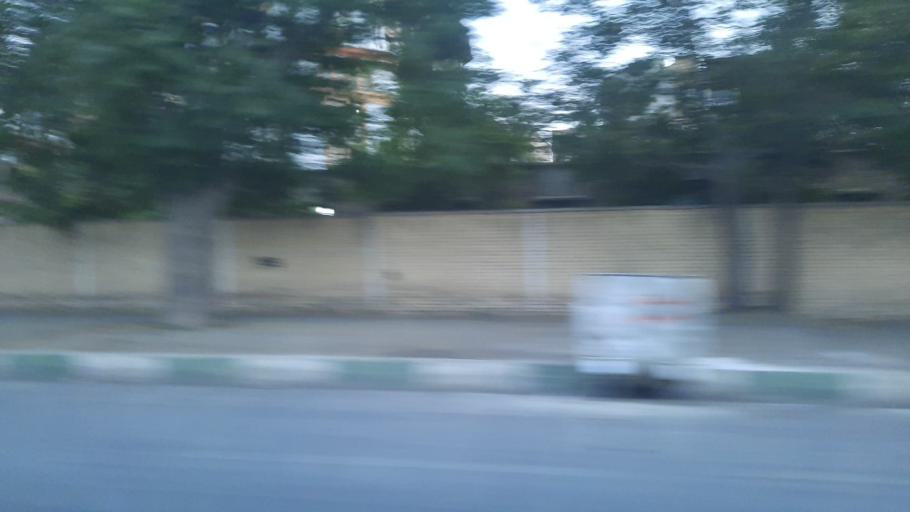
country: IR
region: Markazi
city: Arak
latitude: 34.0752
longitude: 49.7008
